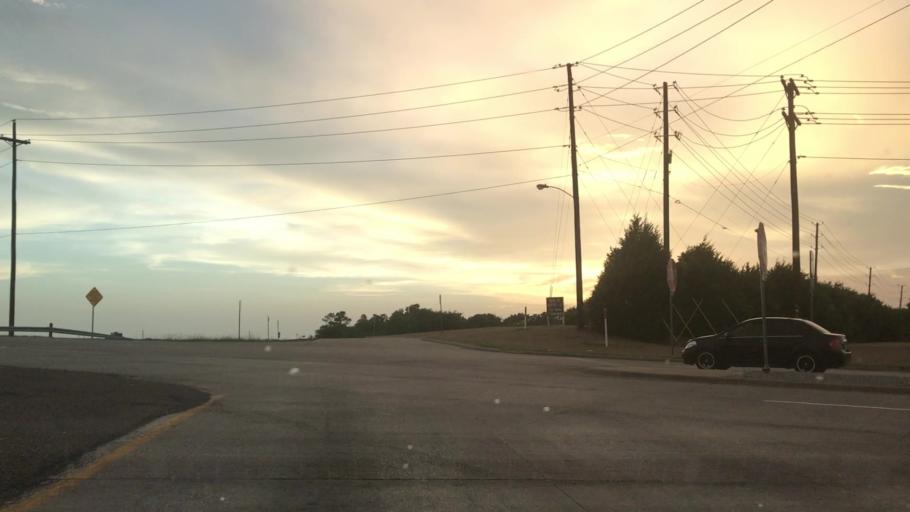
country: US
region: Texas
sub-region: Dallas County
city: Balch Springs
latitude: 32.7043
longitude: -96.5681
